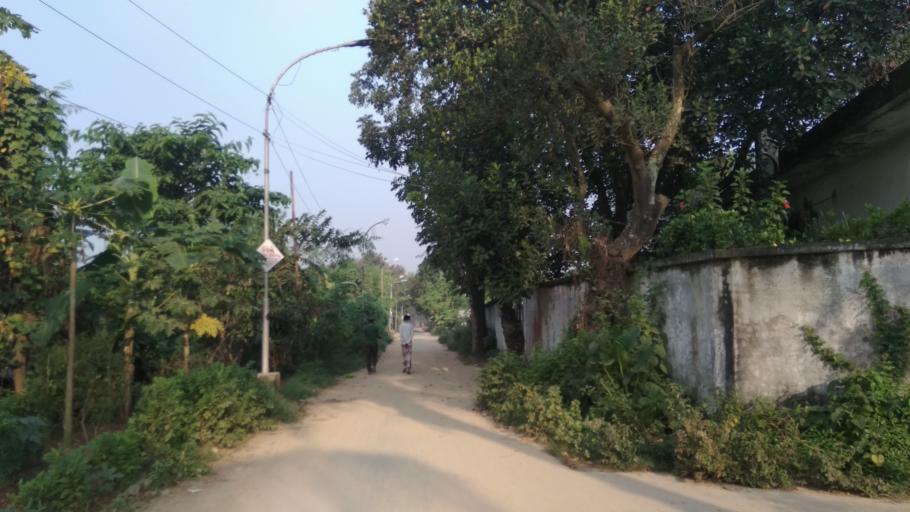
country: BD
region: Dhaka
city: Tungi
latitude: 23.8424
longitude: 90.4193
